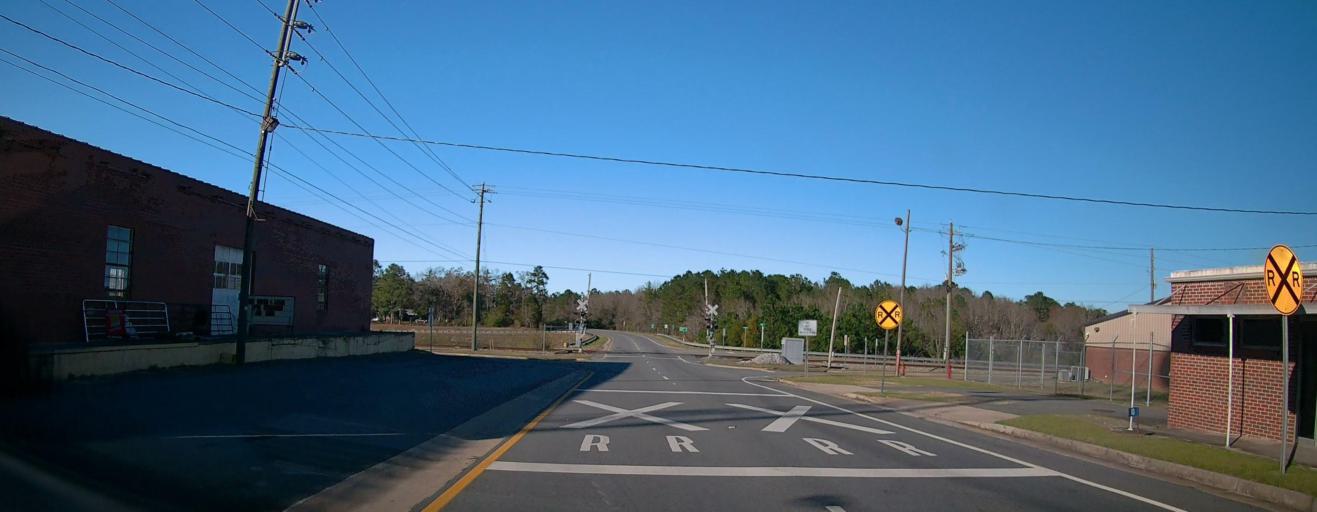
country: US
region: Georgia
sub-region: Taylor County
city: Butler
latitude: 32.5580
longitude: -84.2379
